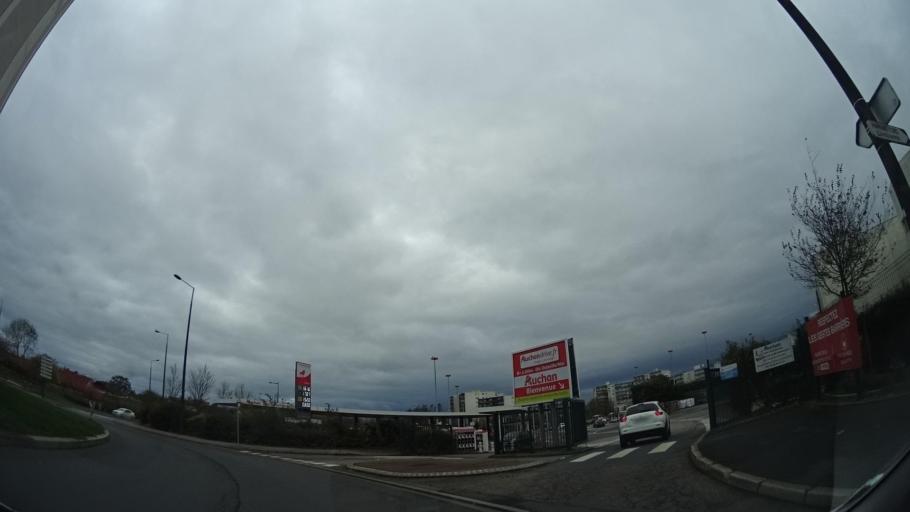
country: FR
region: Haute-Normandie
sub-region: Departement de la Seine-Maritime
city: Sainte-Adresse
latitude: 49.5221
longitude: 0.1093
